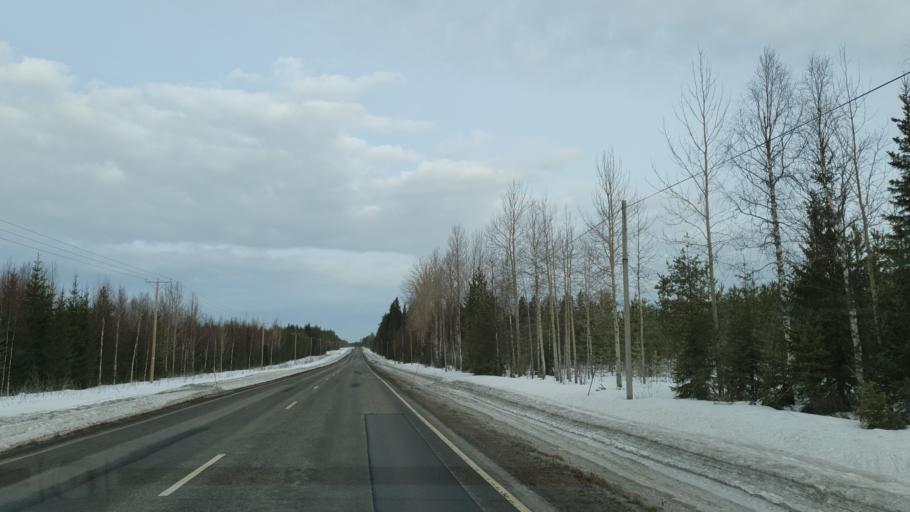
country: FI
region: Kainuu
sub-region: Kajaani
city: Vuokatti
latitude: 64.2070
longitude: 28.1482
